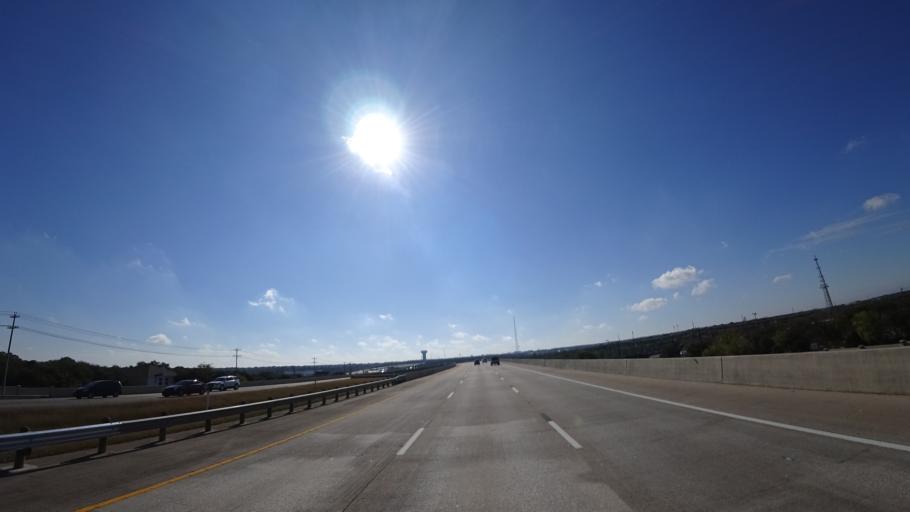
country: US
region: Texas
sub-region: Williamson County
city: Cedar Park
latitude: 30.5054
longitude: -97.8099
